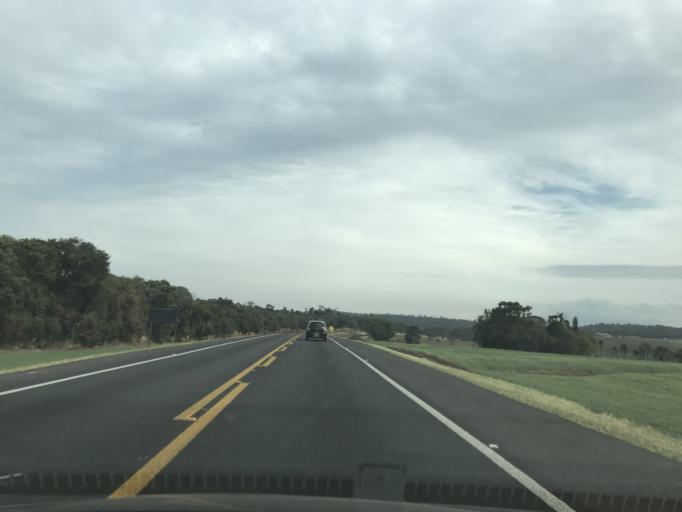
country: BR
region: Parana
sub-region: Matelandia
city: Matelandia
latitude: -25.0986
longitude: -53.7357
